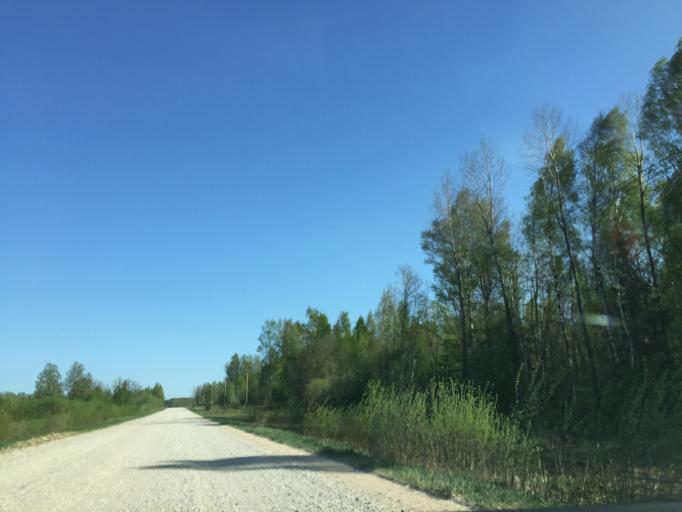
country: LV
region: Skriveri
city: Skriveri
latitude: 56.8436
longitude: 25.0914
